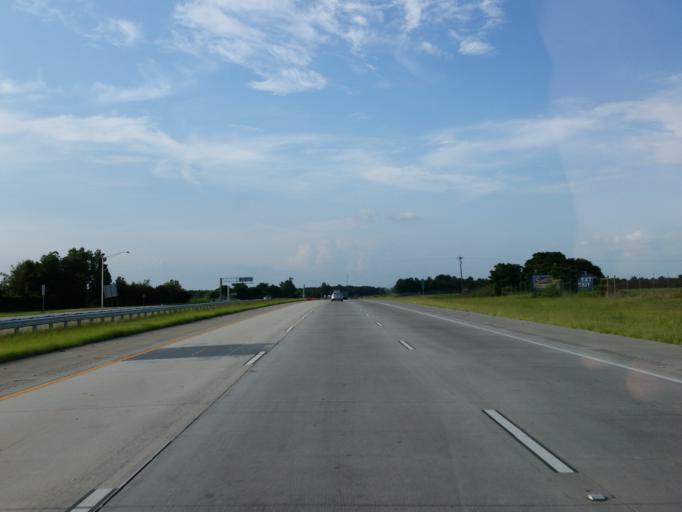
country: US
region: Georgia
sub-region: Dooly County
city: Unadilla
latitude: 32.2104
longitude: -83.7457
